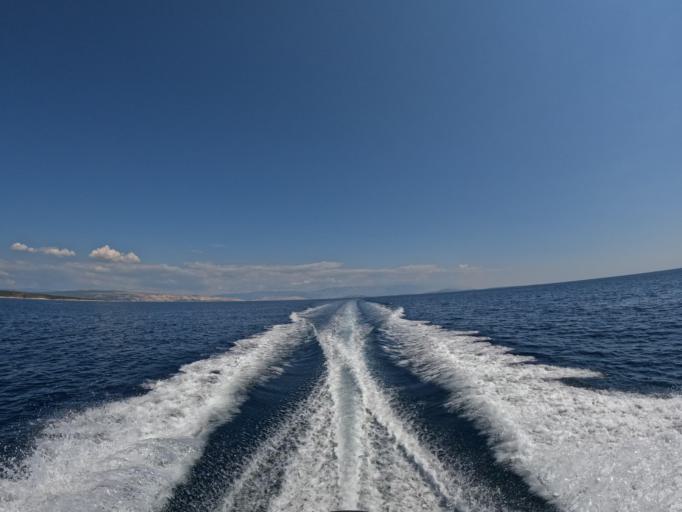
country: HR
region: Primorsko-Goranska
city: Cres
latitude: 44.9393
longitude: 14.4951
